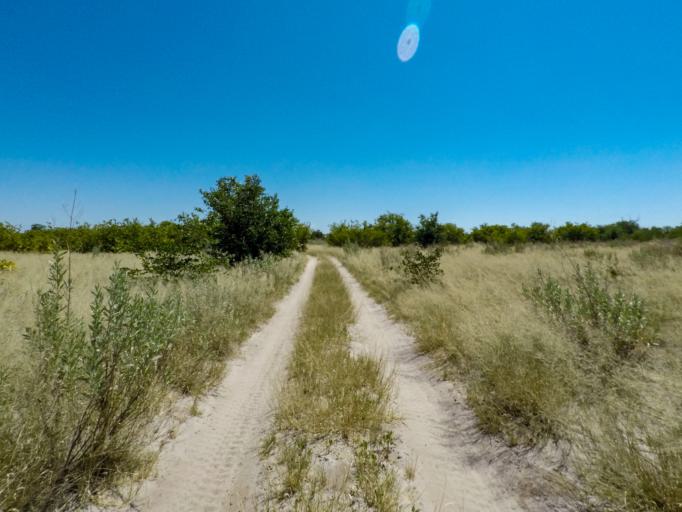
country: BW
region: North West
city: Maun
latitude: -19.4349
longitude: 23.5718
